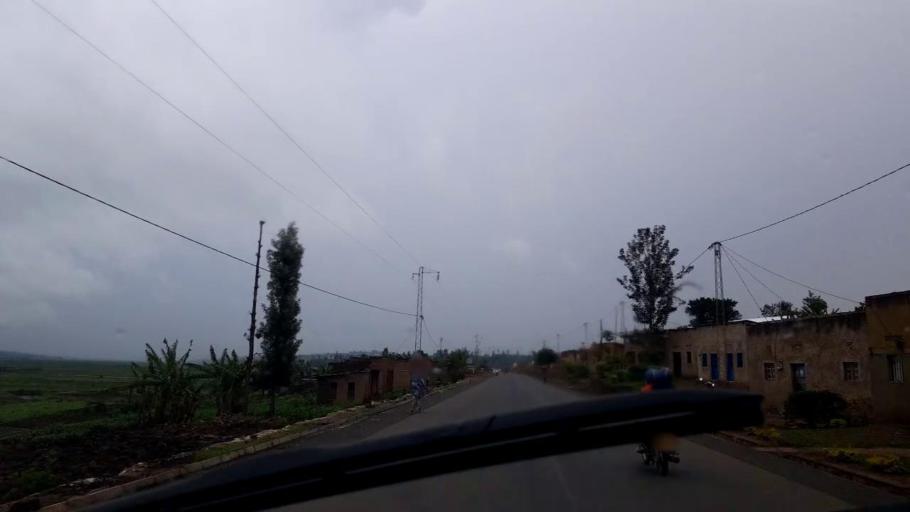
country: RW
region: Northern Province
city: Byumba
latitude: -1.4165
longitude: 30.2799
